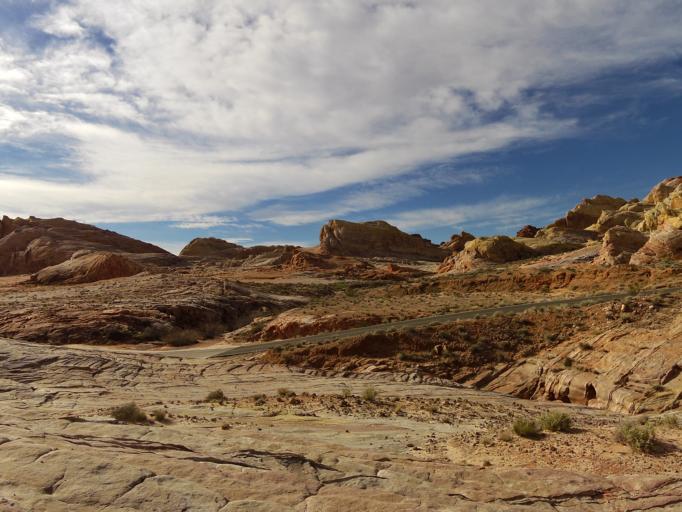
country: US
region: Nevada
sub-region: Clark County
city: Moapa Valley
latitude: 36.4798
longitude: -114.5260
